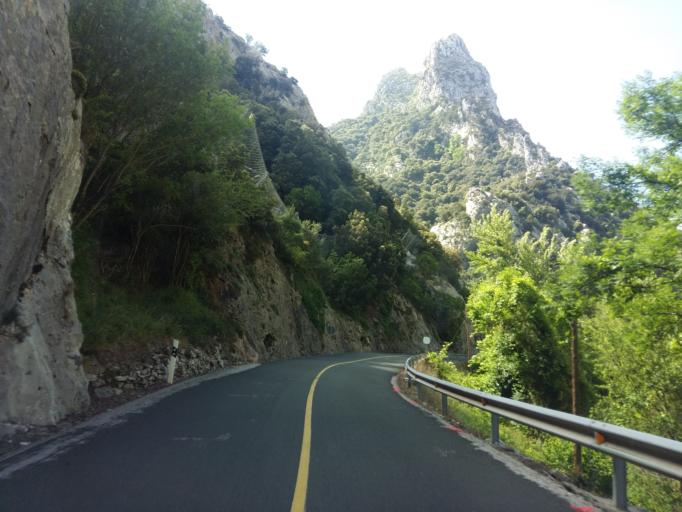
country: ES
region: Cantabria
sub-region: Provincia de Cantabria
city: Potes
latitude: 43.2304
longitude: -4.5817
